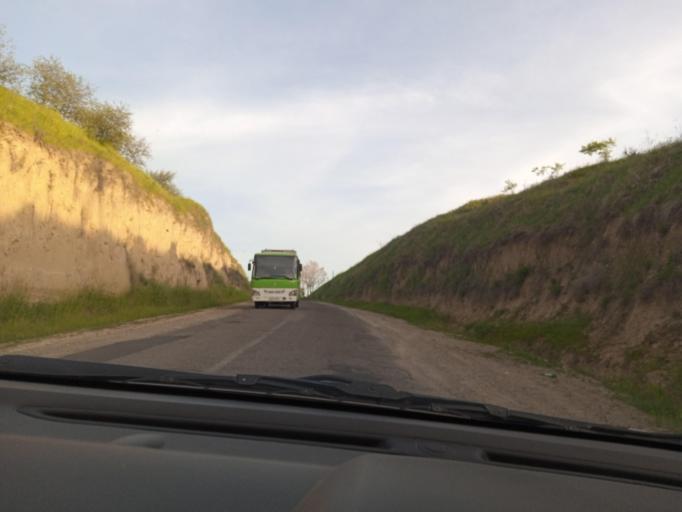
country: UZ
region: Toshkent
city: Parkent
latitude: 41.2393
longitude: 69.7333
